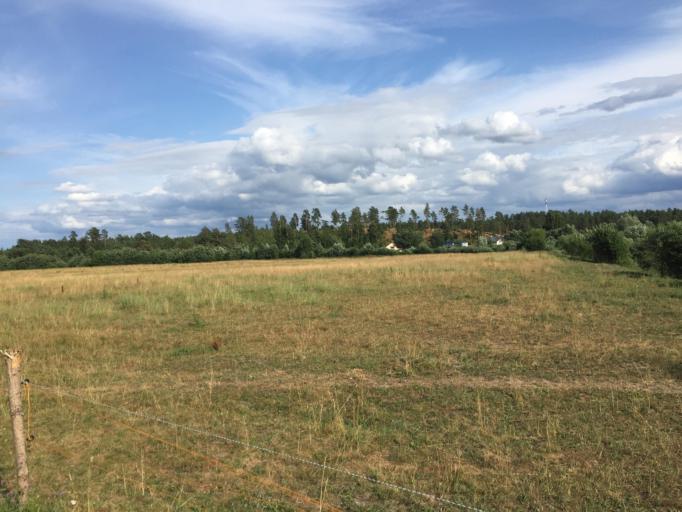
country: LV
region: Adazi
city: Adazi
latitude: 57.0628
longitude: 24.3424
